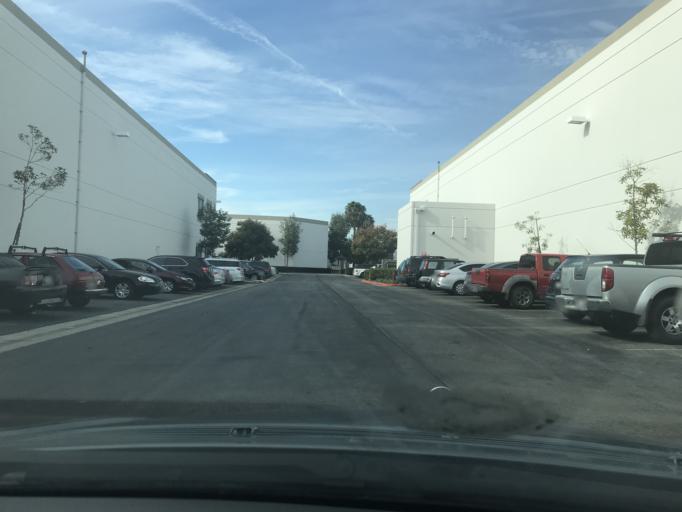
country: US
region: California
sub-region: Los Angeles County
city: Santa Fe Springs
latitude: 33.9334
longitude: -118.0616
